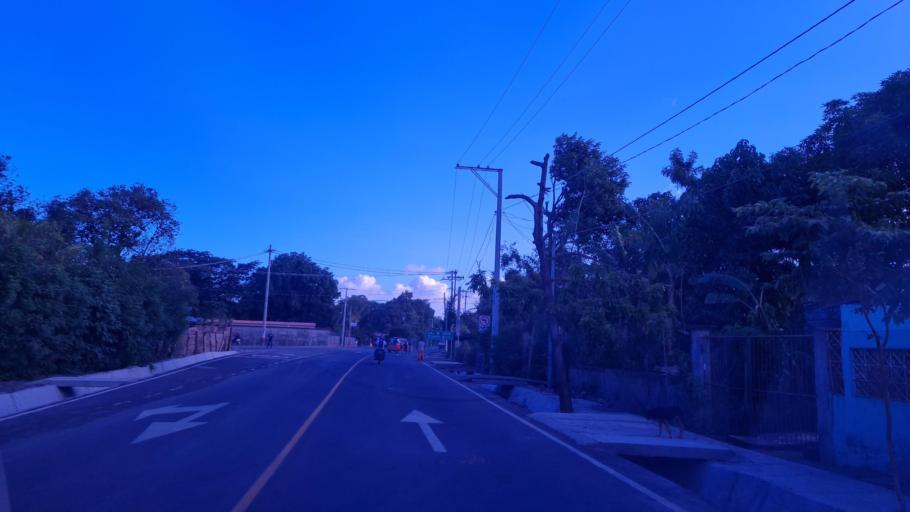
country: NI
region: Masaya
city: Ticuantepe
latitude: 12.0888
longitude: -86.1656
